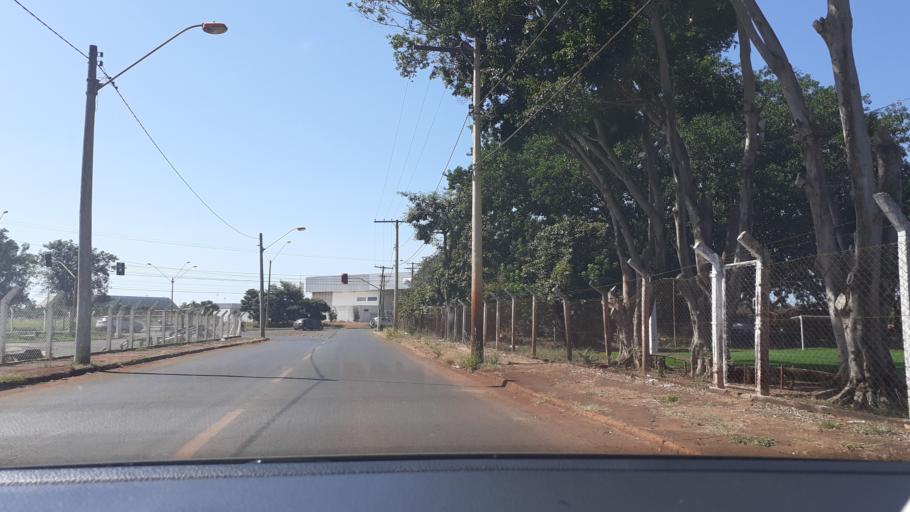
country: BR
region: Goias
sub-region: Itumbiara
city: Itumbiara
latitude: -18.4114
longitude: -49.2495
